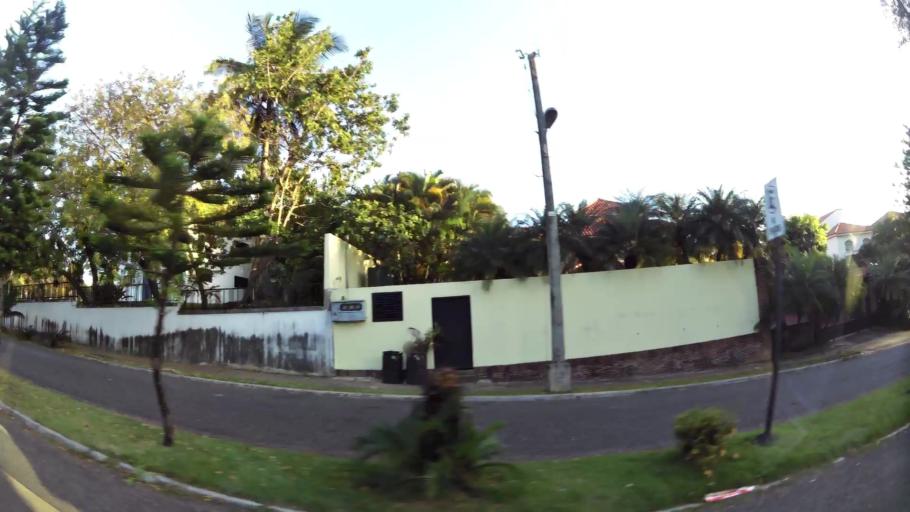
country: DO
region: Nacional
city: La Agustina
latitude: 18.4917
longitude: -69.9599
